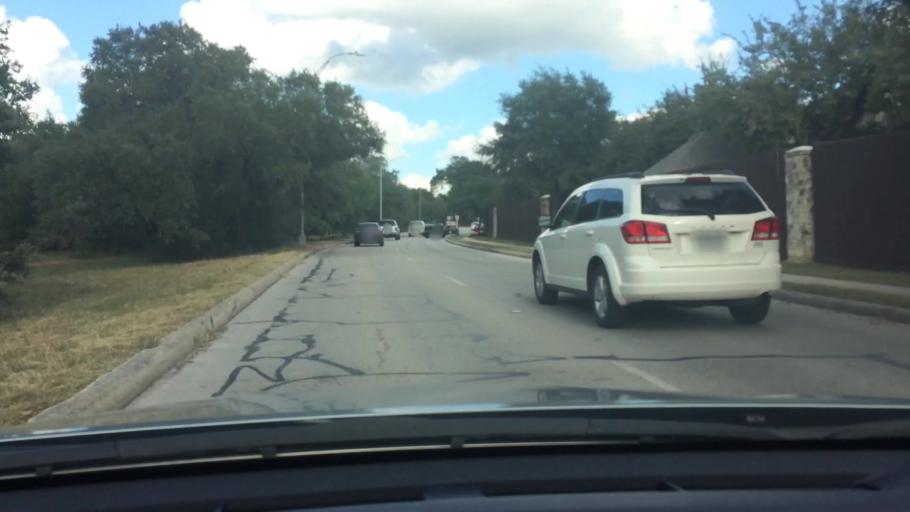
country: US
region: Texas
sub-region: Bexar County
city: Hollywood Park
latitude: 29.6467
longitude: -98.4333
